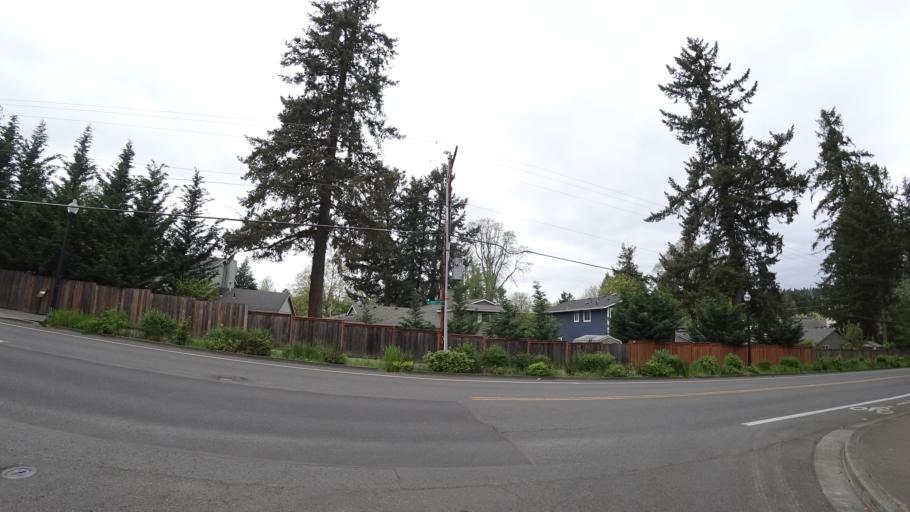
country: US
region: Oregon
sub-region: Washington County
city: Beaverton
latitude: 45.4635
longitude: -122.8362
